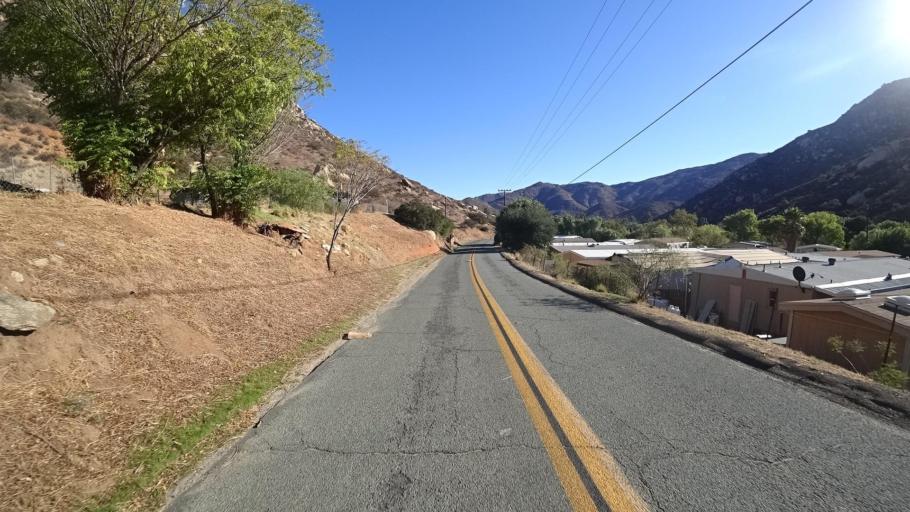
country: MX
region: Baja California
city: Tecate
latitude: 32.6232
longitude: -116.6917
